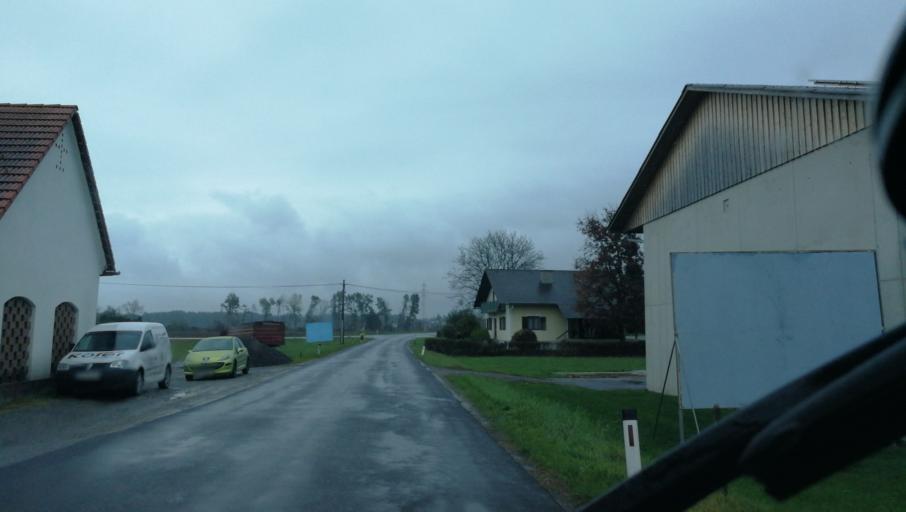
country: AT
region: Styria
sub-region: Politischer Bezirk Leibnitz
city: Spielfeld
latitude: 46.7161
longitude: 15.6417
